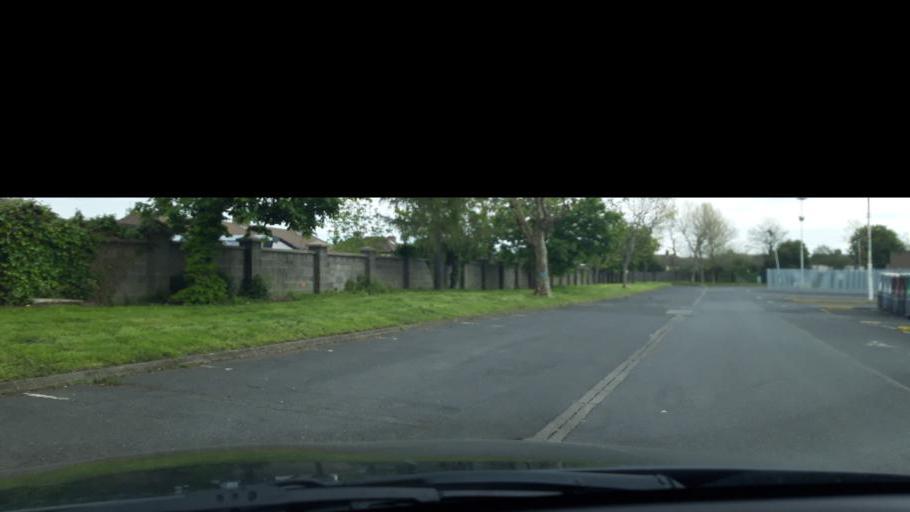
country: IE
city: Greenhills
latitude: 53.3312
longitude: -6.3021
